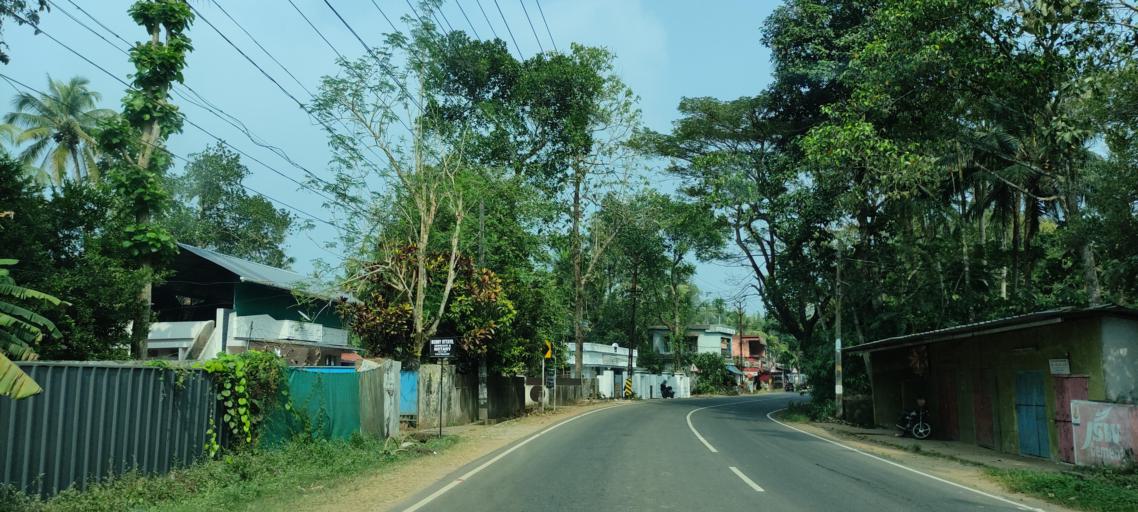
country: IN
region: Kerala
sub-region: Kottayam
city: Vaikam
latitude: 9.7676
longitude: 76.4162
